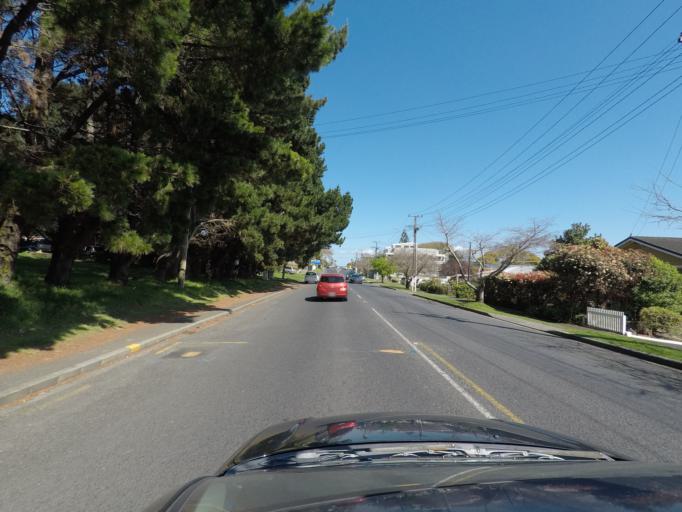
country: NZ
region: Auckland
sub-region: Auckland
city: Tamaki
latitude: -36.9273
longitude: 174.8449
